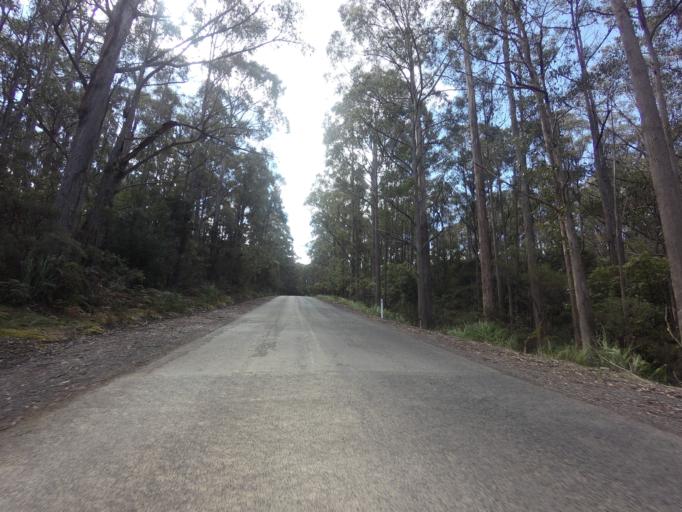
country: AU
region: Tasmania
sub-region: Huon Valley
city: Geeveston
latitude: -43.4161
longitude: 146.9094
